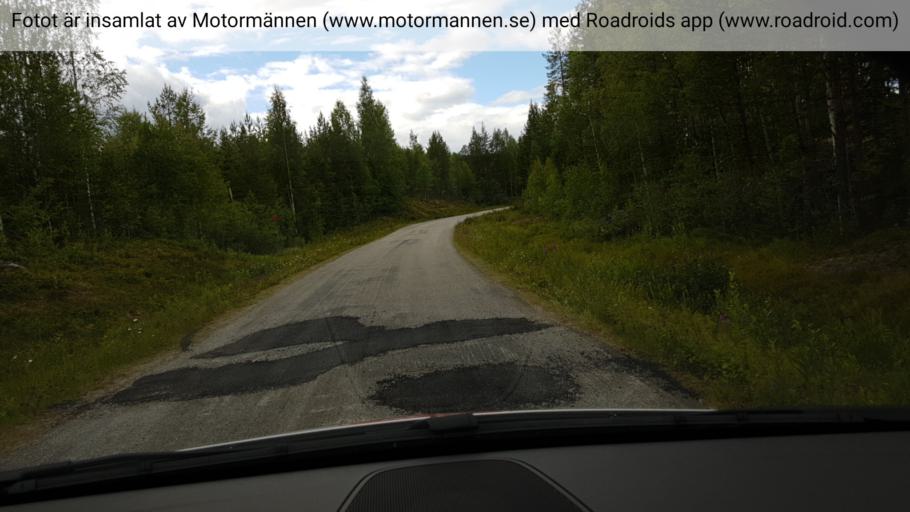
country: SE
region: Vaesterbotten
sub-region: Dorotea Kommun
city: Dorotea
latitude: 63.9119
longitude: 16.2716
